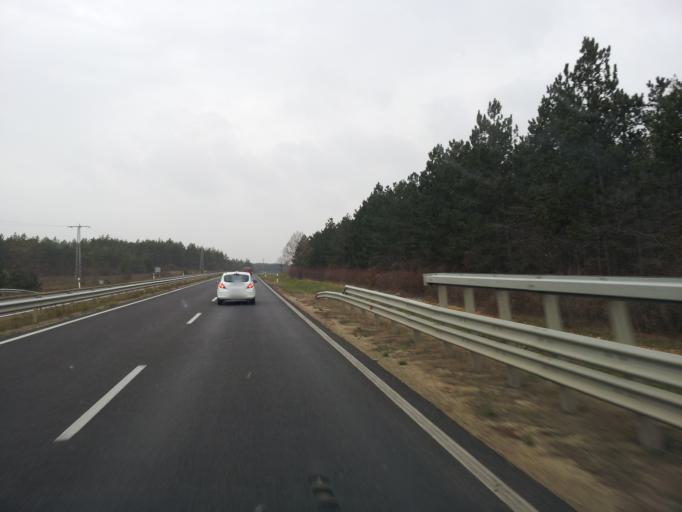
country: HU
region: Veszprem
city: Nemesvamos
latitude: 47.1145
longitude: 17.8484
